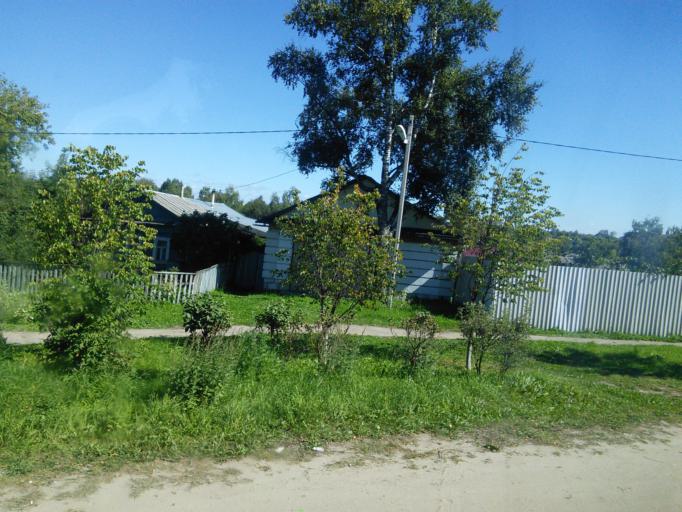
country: RU
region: Tverskaya
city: Kashin
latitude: 57.3615
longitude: 37.6139
